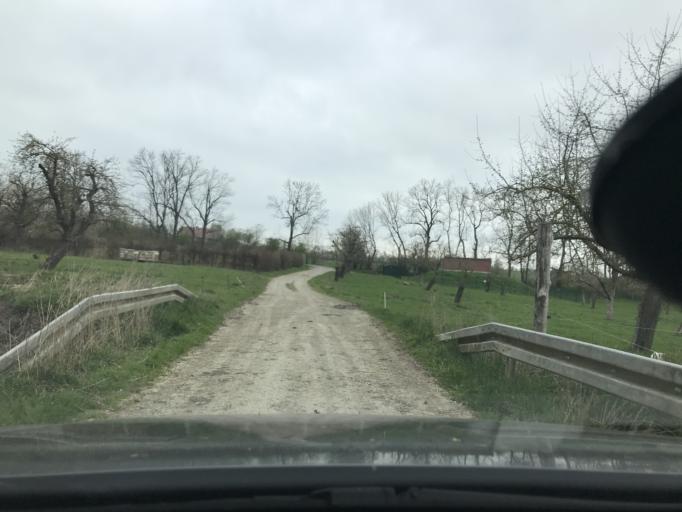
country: DE
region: Thuringia
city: Muehlhausen
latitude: 51.2228
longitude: 10.4247
